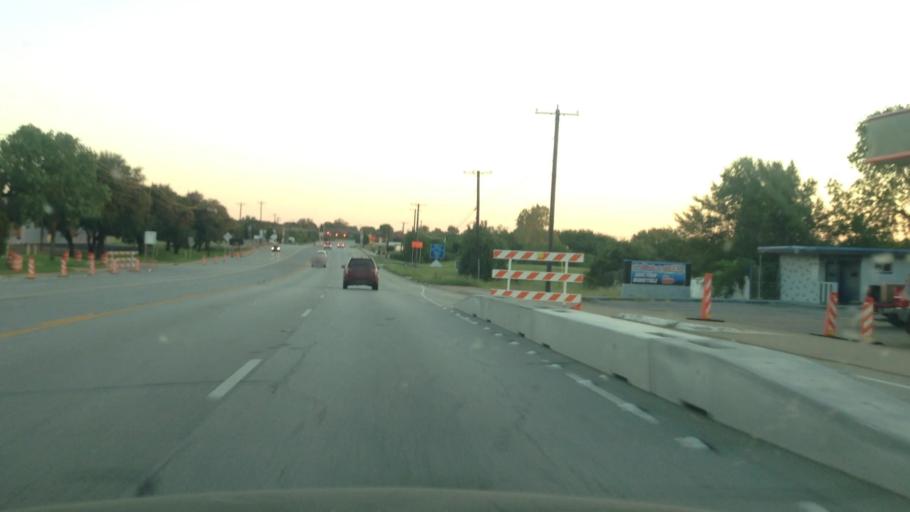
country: US
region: Texas
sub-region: Tarrant County
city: North Richland Hills
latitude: 32.8634
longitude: -97.2087
